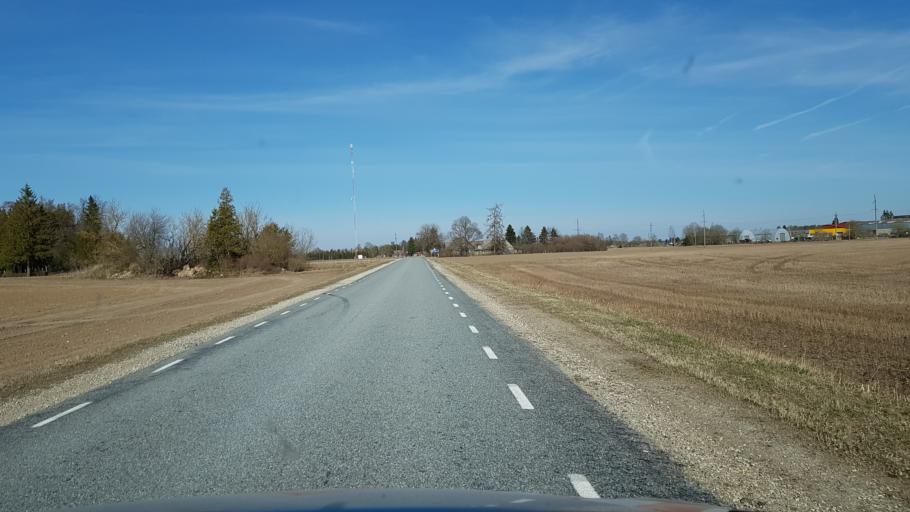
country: EE
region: Laeaene-Virumaa
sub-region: Rakke vald
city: Rakke
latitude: 59.0465
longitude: 26.3740
